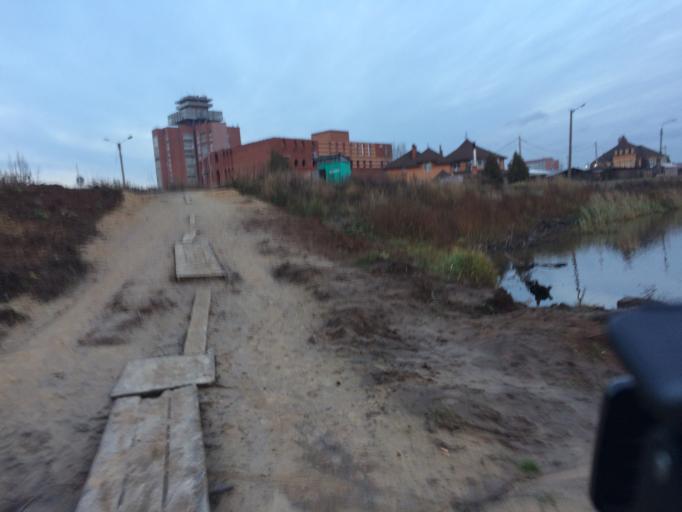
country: RU
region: Mariy-El
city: Yoshkar-Ola
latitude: 56.6260
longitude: 47.9014
